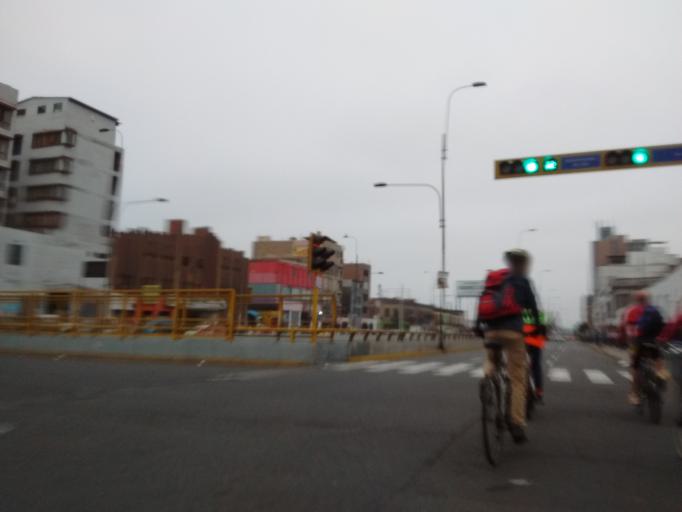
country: PE
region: Lima
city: Lima
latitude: -12.0591
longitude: -77.0314
